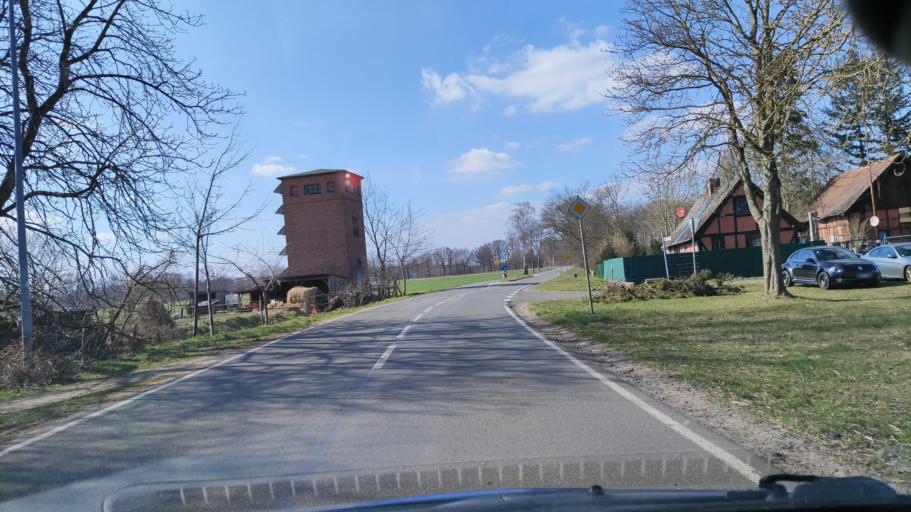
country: DE
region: Lower Saxony
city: Trebel
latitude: 53.0322
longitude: 11.2979
